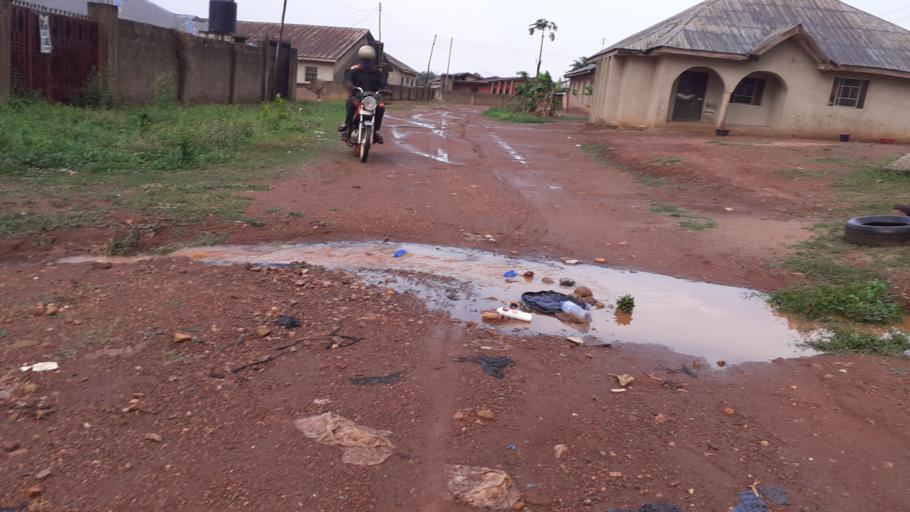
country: NG
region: Ondo
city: Akure
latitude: 7.2150
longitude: 5.2158
